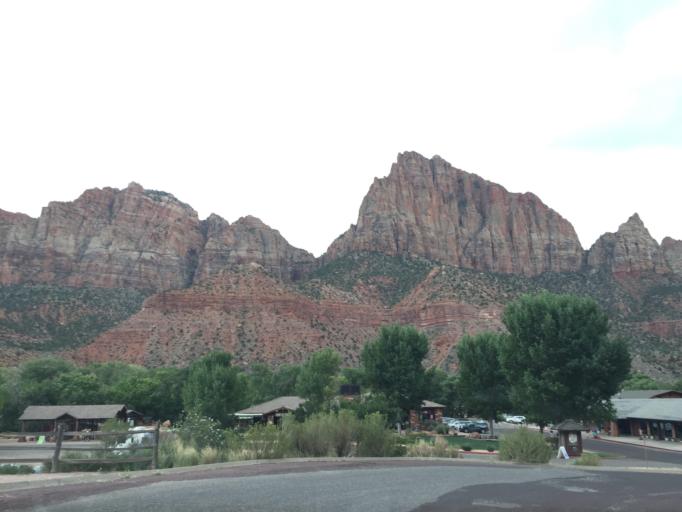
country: US
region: Utah
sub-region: Washington County
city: Hildale
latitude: 37.2000
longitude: -112.9898
